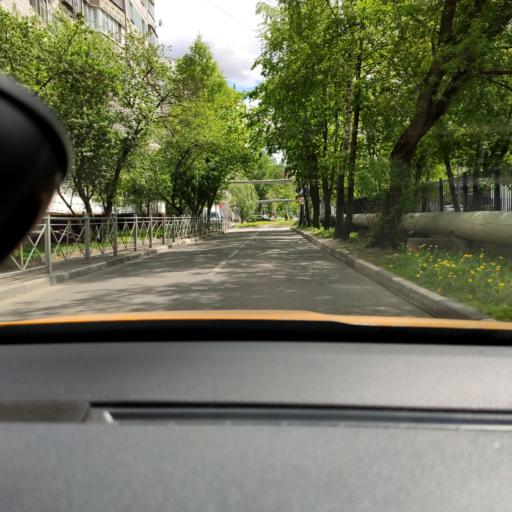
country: RU
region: Moskovskaya
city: Novopodrezkovo
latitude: 55.9424
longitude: 37.3446
